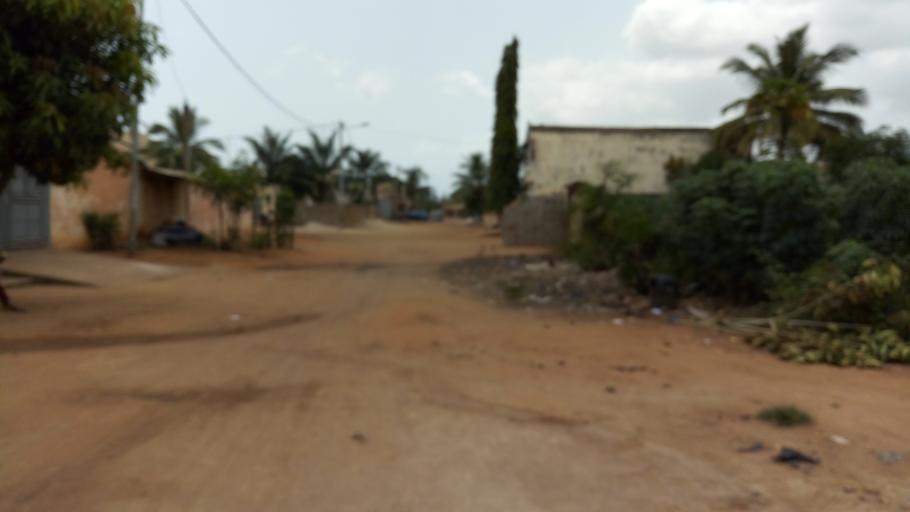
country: TG
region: Maritime
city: Lome
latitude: 6.2240
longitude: 1.1660
